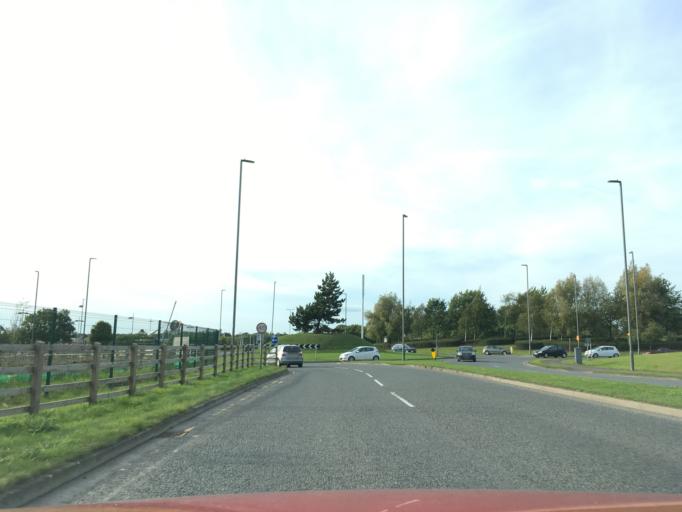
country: GB
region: England
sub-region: South Gloucestershire
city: Almondsbury
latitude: 51.5228
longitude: -2.5985
